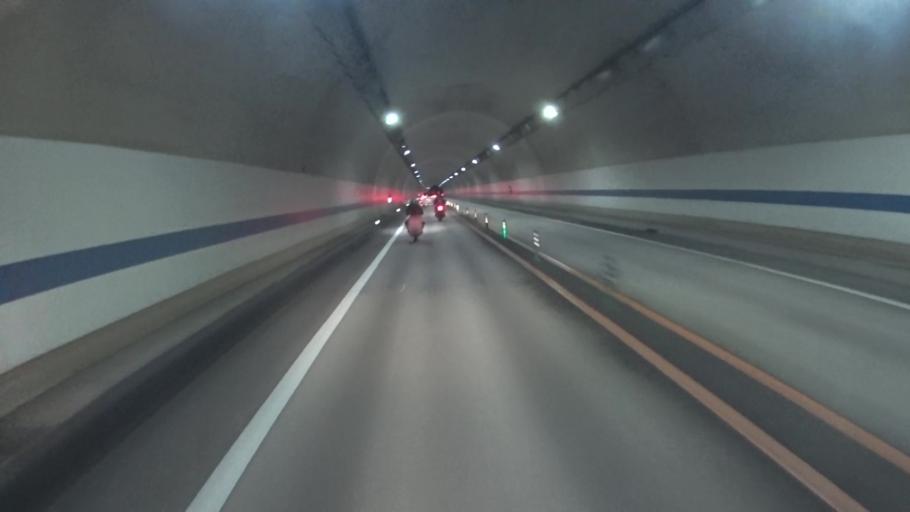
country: JP
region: Kyoto
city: Ayabe
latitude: 35.3678
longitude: 135.2833
